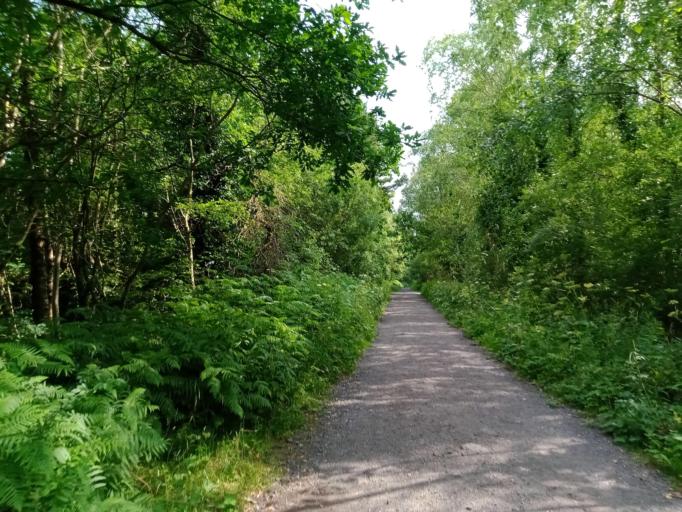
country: IE
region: Leinster
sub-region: Laois
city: Abbeyleix
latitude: 52.9021
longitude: -7.3509
